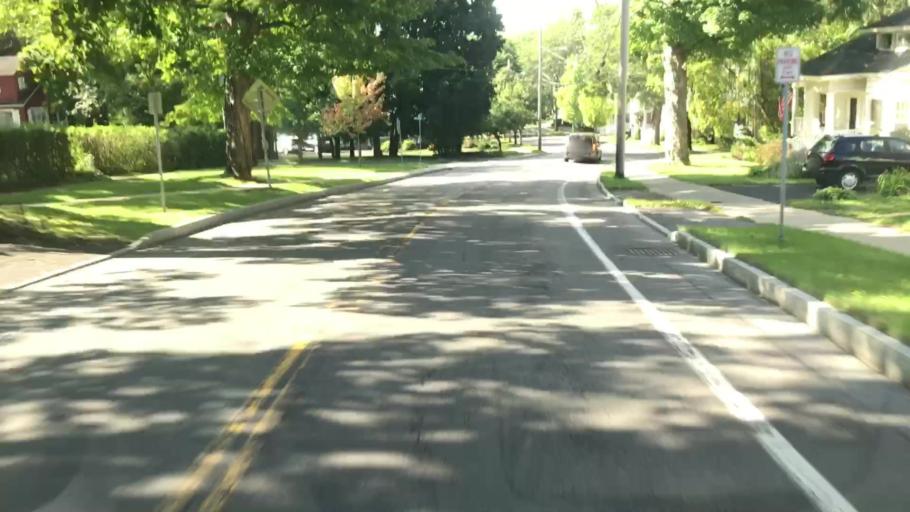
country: US
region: New York
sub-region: Onondaga County
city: Skaneateles
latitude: 42.9488
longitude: -76.4269
